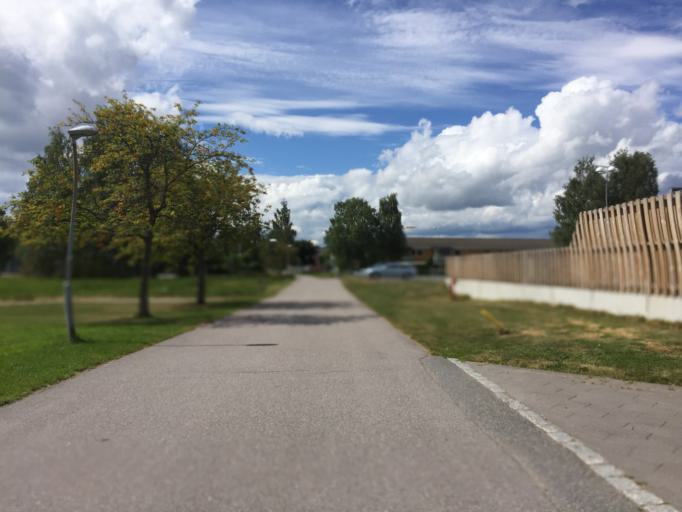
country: SE
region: OErebro
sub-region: Orebro Kommun
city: Orebro
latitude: 59.2746
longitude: 15.1642
